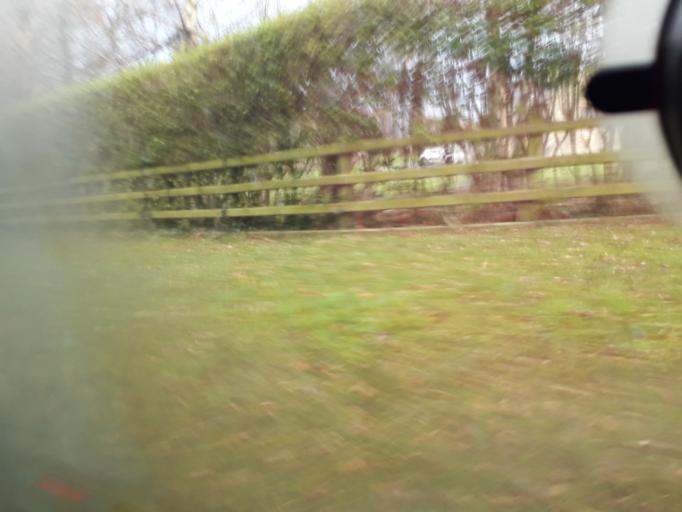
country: IE
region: Leinster
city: Ballyboden
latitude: 53.2493
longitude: -6.3000
